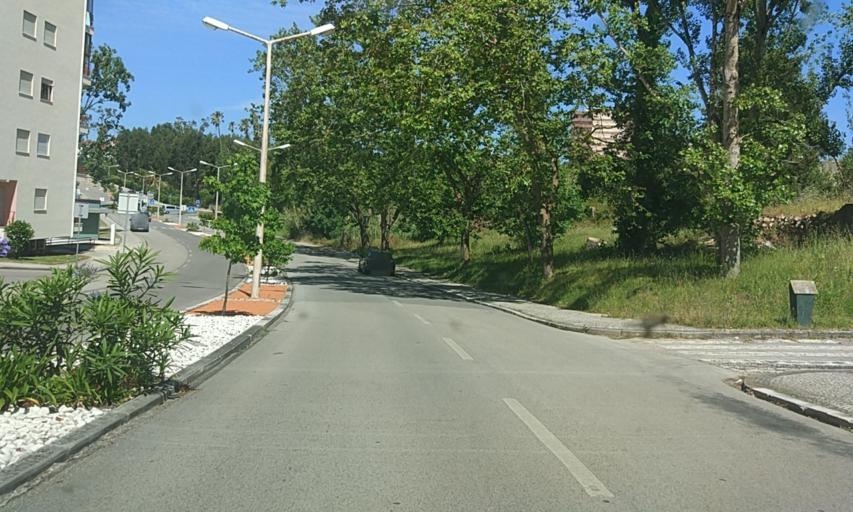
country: PT
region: Coimbra
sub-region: Figueira da Foz
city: Figueira da Foz
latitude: 40.1549
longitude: -8.8592
